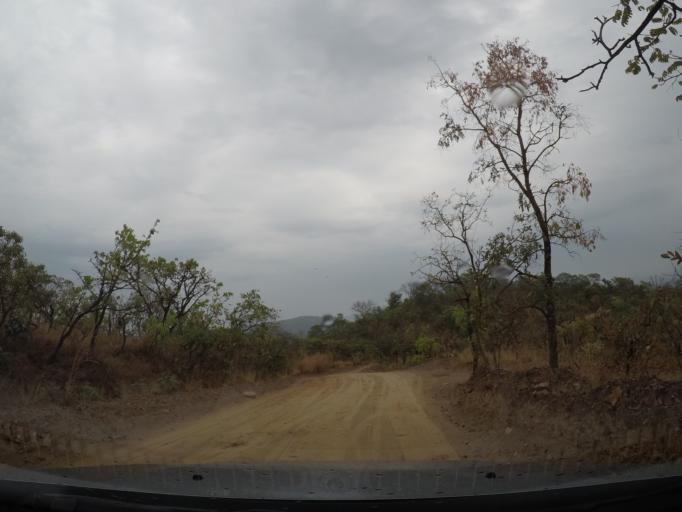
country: BR
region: Goias
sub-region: Pirenopolis
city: Pirenopolis
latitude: -15.8394
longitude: -48.9155
